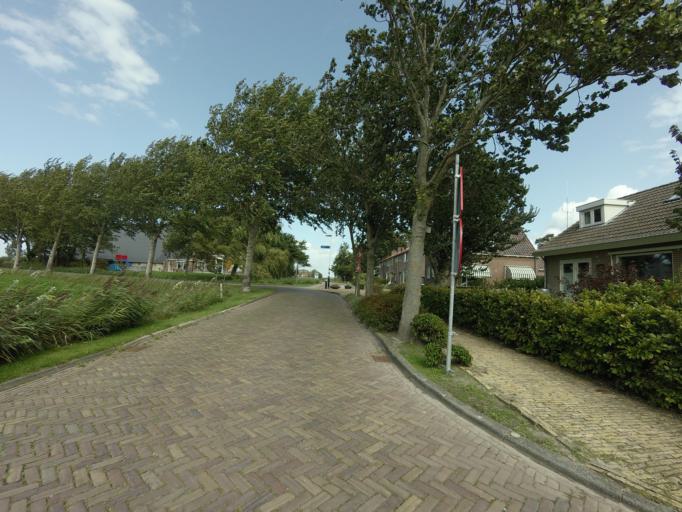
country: NL
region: Friesland
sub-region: Gemeente Harlingen
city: Harlingen
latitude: 53.1168
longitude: 5.4378
